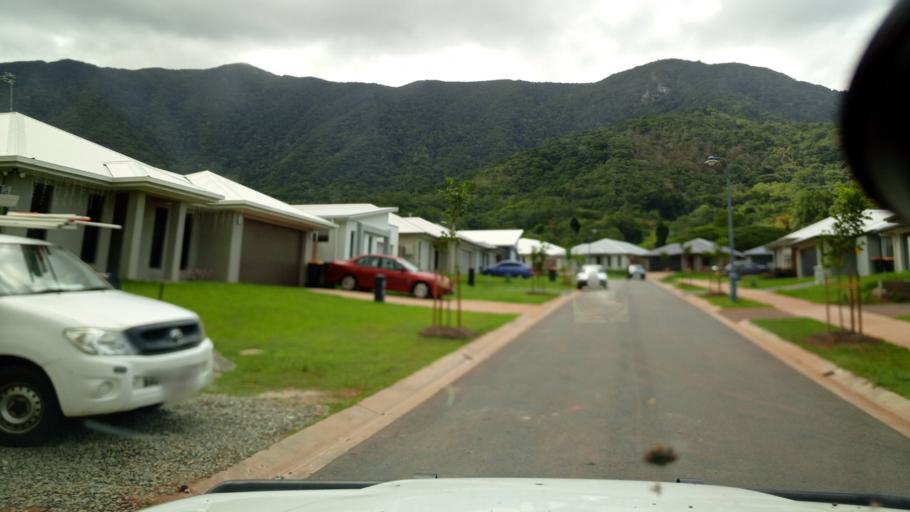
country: AU
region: Queensland
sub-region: Cairns
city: Redlynch
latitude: -16.8978
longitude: 145.6940
